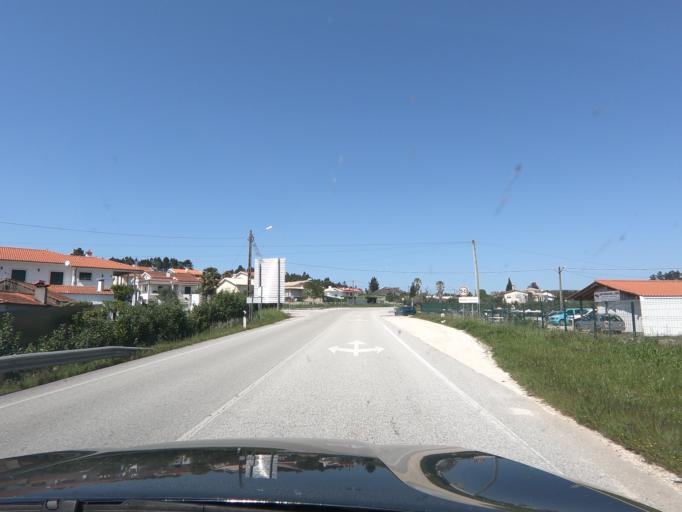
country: PT
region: Coimbra
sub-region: Vila Nova de Poiares
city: Poiares
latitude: 40.1794
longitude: -8.2646
